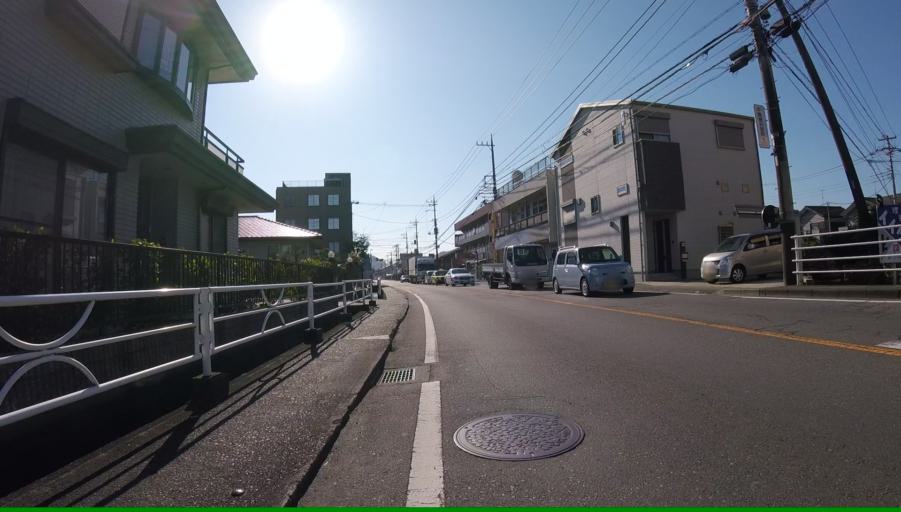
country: JP
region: Shizuoka
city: Mishima
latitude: 35.0937
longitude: 138.9164
